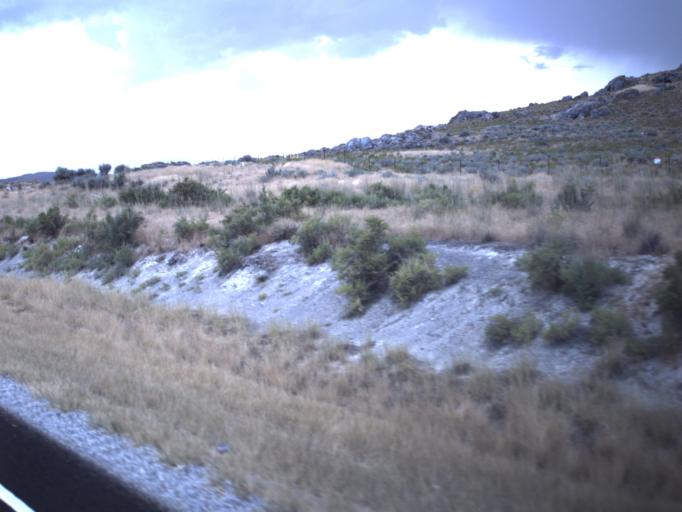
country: US
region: Utah
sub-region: Box Elder County
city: Tremonton
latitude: 41.6302
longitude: -112.4167
